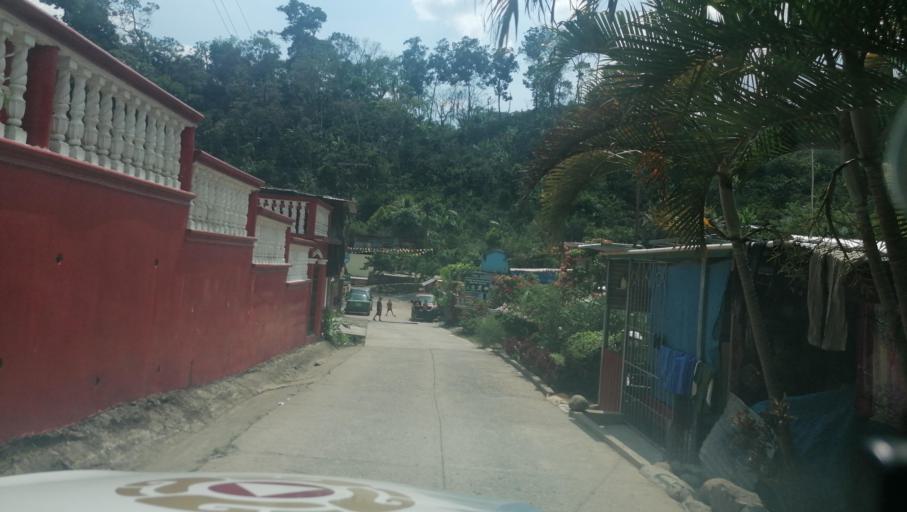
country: MX
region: Chiapas
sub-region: Cacahoatan
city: Benito Juarez
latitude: 15.0360
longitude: -92.2365
